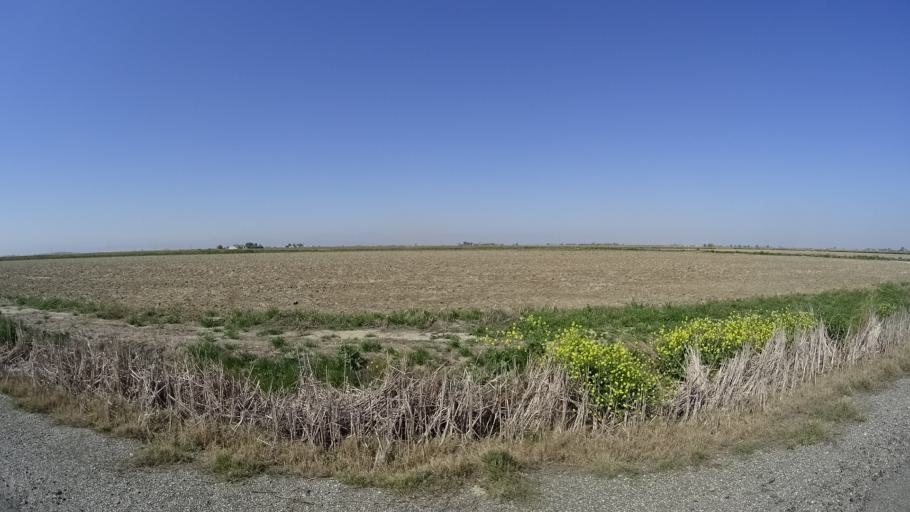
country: US
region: California
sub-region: Glenn County
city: Willows
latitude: 39.4971
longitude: -122.0653
